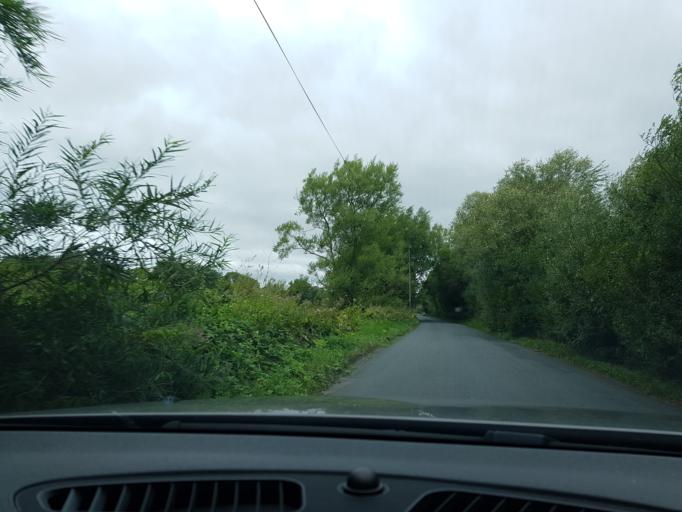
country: GB
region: England
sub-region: Wiltshire
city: Ramsbury
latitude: 51.4403
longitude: -1.5840
